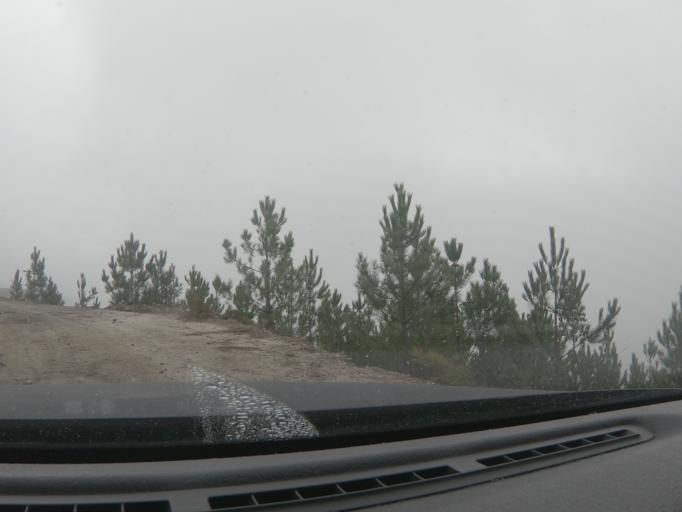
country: PT
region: Vila Real
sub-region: Vila Real
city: Vila Real
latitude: 41.3740
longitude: -7.7439
